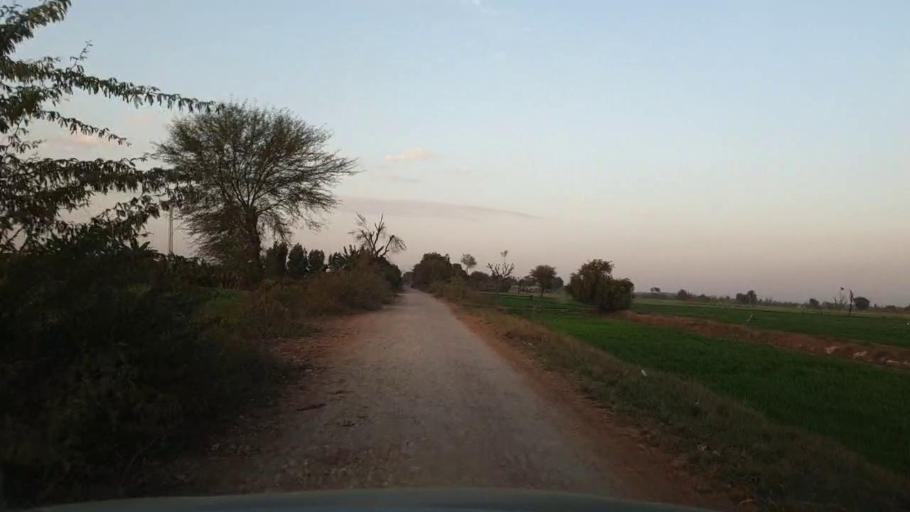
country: PK
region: Sindh
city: Matiari
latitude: 25.6045
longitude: 68.4808
